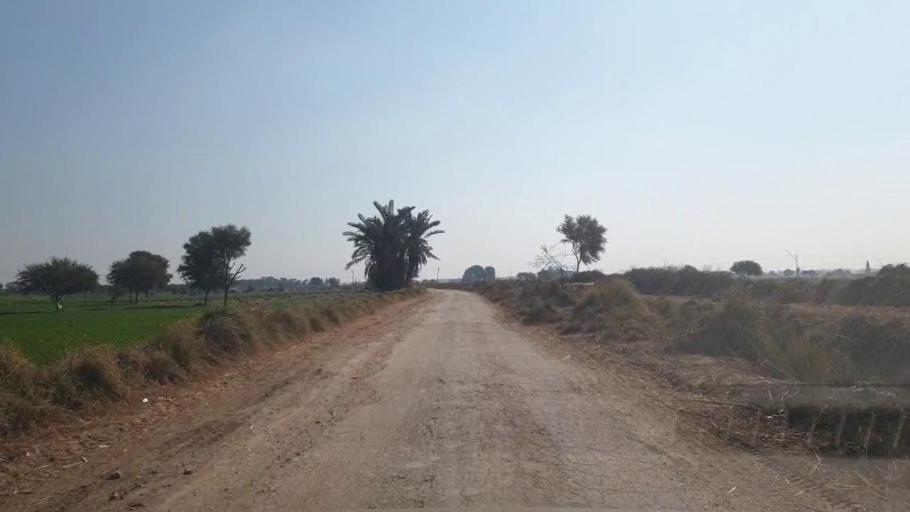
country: PK
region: Sindh
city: Shahdadpur
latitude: 25.9456
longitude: 68.6349
